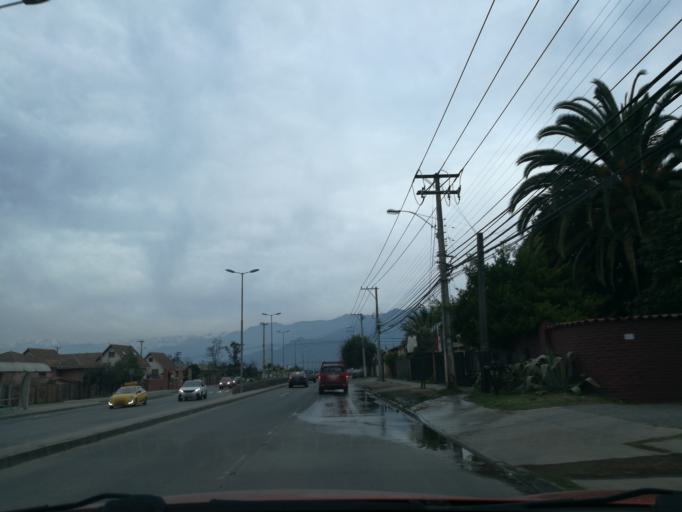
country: CL
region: O'Higgins
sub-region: Provincia de Cachapoal
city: Machali
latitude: -34.1732
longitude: -70.6875
